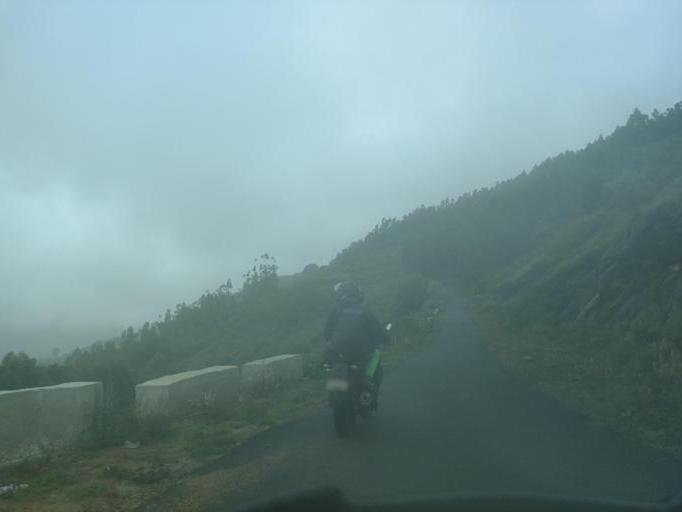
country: IN
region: Tamil Nadu
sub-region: Dindigul
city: Kodaikanal
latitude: 10.2317
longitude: 77.3331
